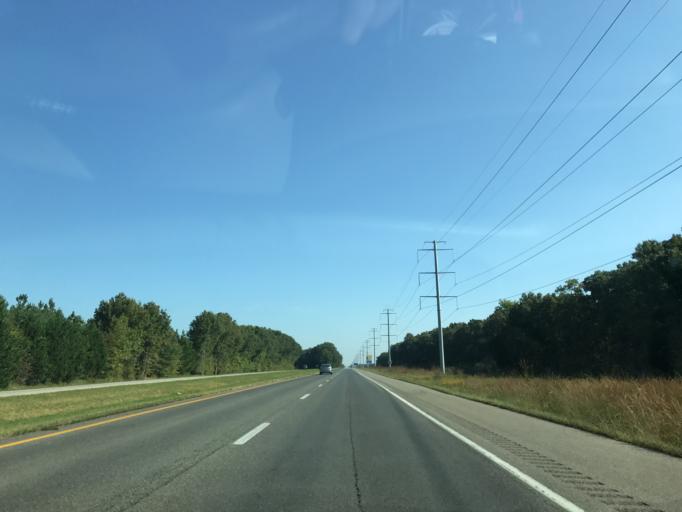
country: US
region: Maryland
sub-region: Queen Anne's County
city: Centreville
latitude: 39.0682
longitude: -75.9877
